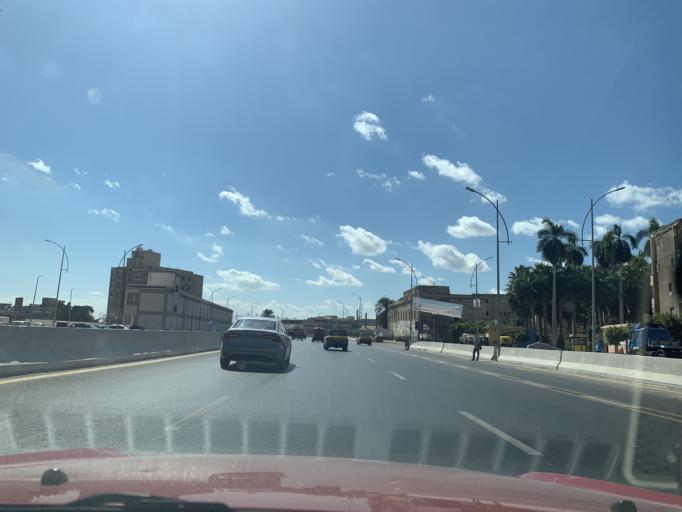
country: EG
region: Alexandria
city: Alexandria
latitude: 31.1926
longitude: 29.9311
